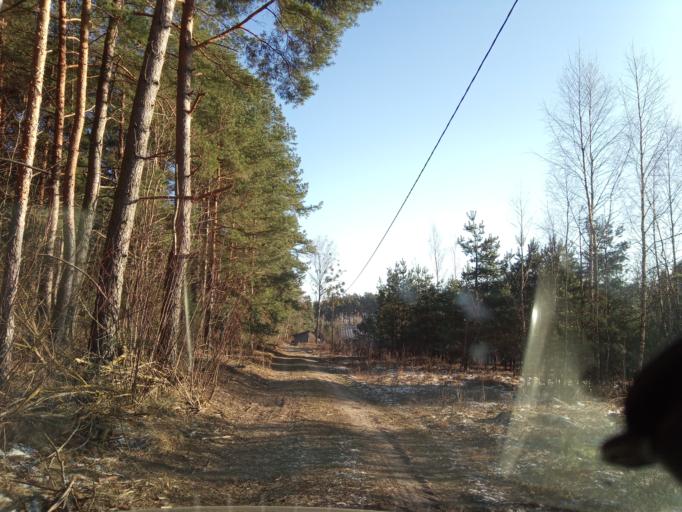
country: LT
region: Alytaus apskritis
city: Druskininkai
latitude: 53.9486
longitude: 23.8757
